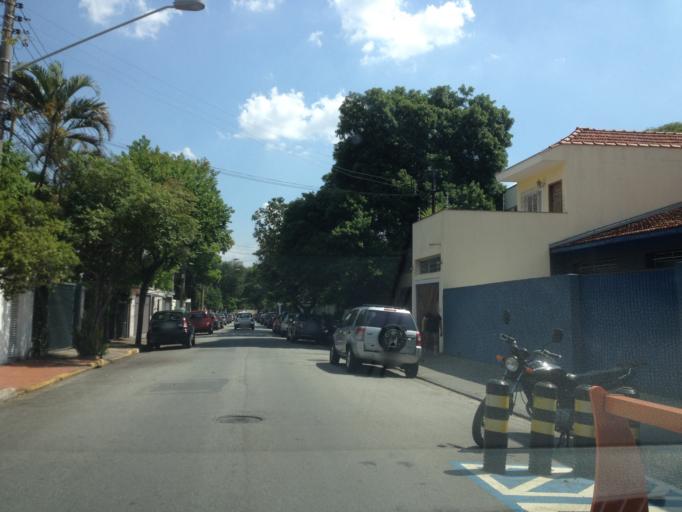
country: BR
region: Sao Paulo
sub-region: Sao Paulo
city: Sao Paulo
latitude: -23.5686
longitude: -46.6778
